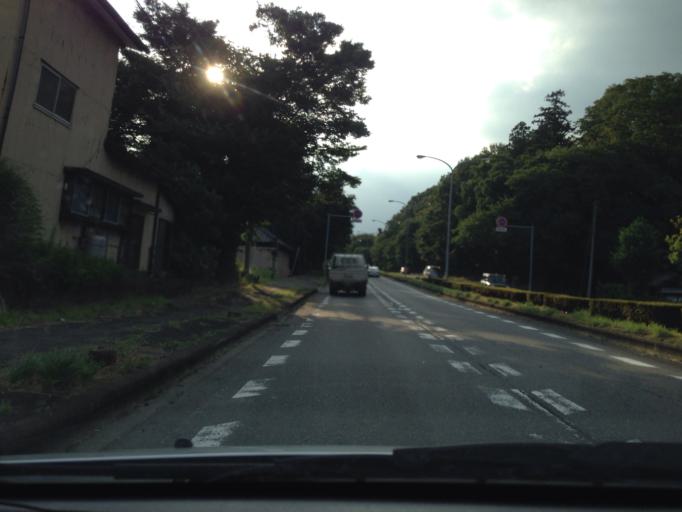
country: JP
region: Ibaraki
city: Naka
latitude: 36.0847
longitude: 140.1625
